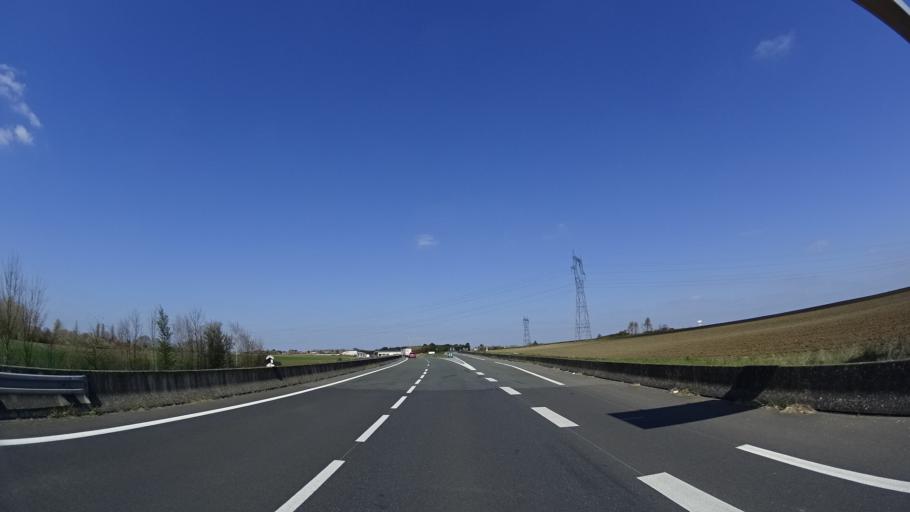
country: FR
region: Pays de la Loire
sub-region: Departement de Maine-et-Loire
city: Doue-la-Fontaine
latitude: 47.2278
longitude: -0.3084
